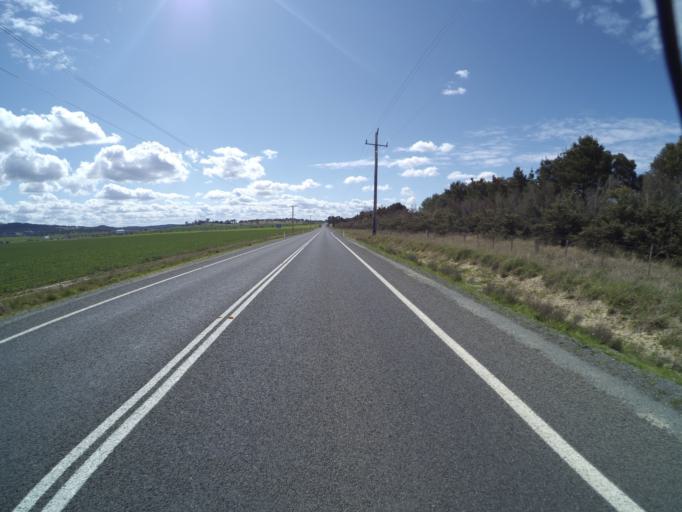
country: AU
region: New South Wales
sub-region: Goulburn Mulwaree
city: Goulburn
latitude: -34.8433
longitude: 149.6832
